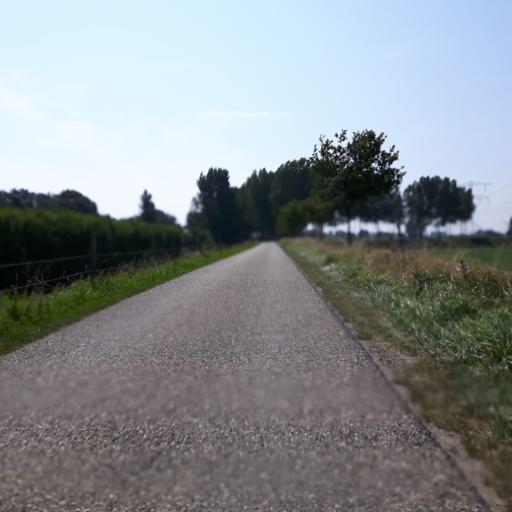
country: NL
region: Zeeland
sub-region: Gemeente Goes
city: Goes
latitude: 51.4563
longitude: 3.9273
